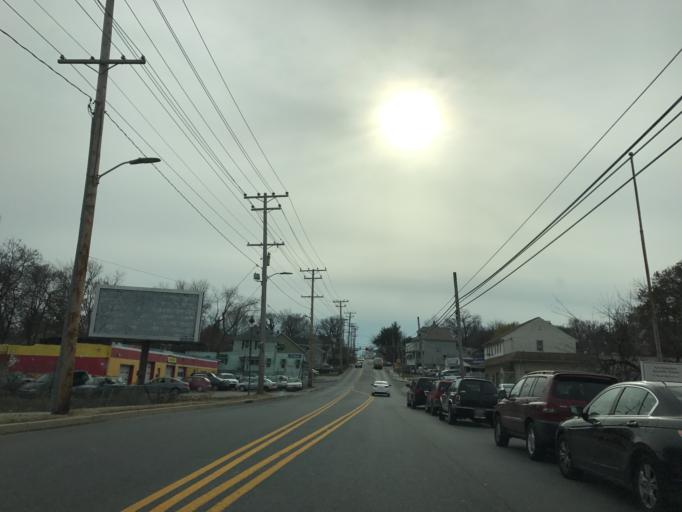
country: US
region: Maryland
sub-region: Baltimore County
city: Baltimore Highlands
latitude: 39.2468
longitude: -76.6404
